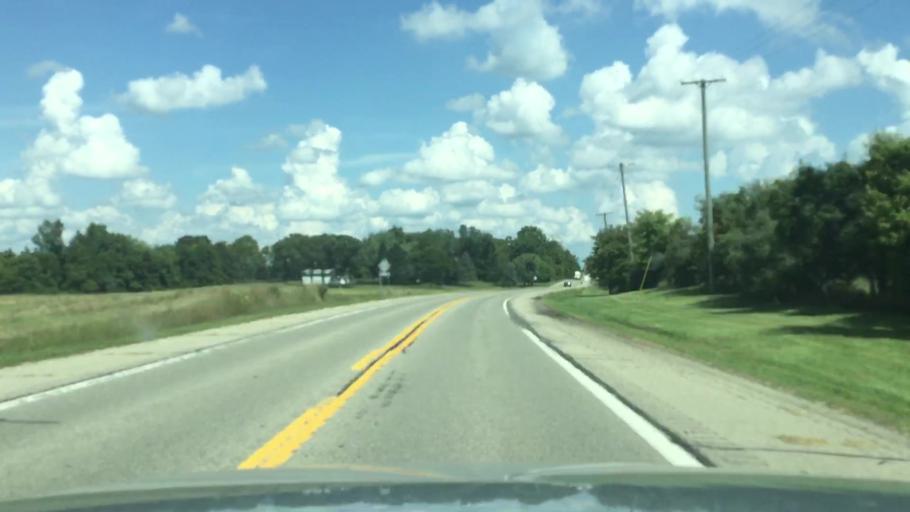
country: US
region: Michigan
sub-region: Lenawee County
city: Clinton
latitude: 42.0841
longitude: -83.9465
